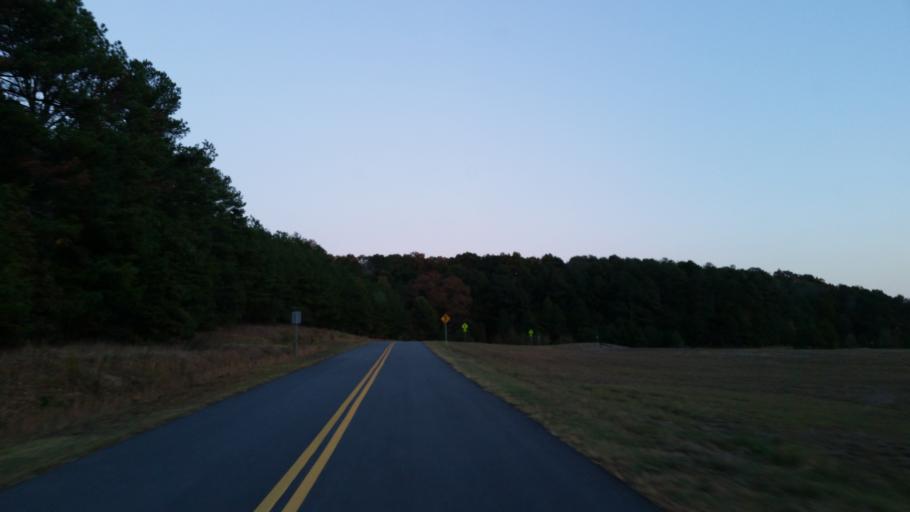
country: US
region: Georgia
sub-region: Gordon County
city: Calhoun
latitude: 34.5939
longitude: -84.9613
